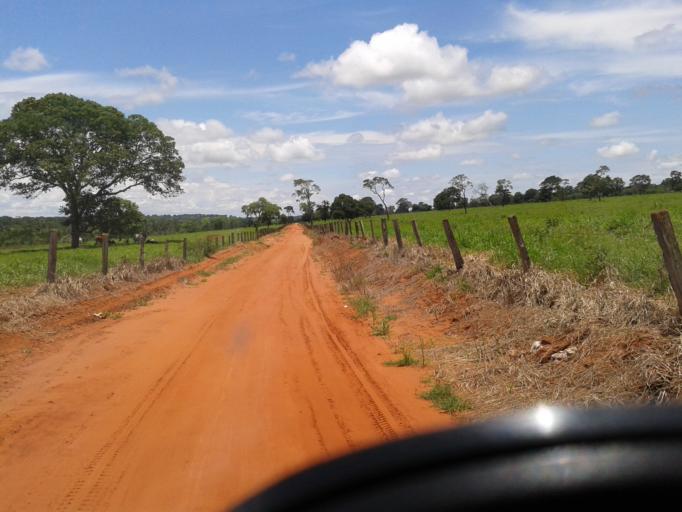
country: BR
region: Minas Gerais
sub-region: Santa Vitoria
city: Santa Vitoria
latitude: -18.9448
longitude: -49.8617
